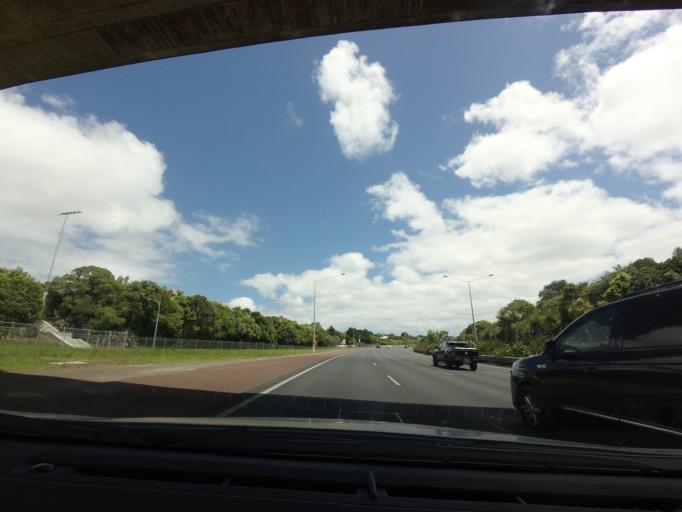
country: NZ
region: Auckland
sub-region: Auckland
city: Auckland
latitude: -36.8686
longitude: 174.7460
